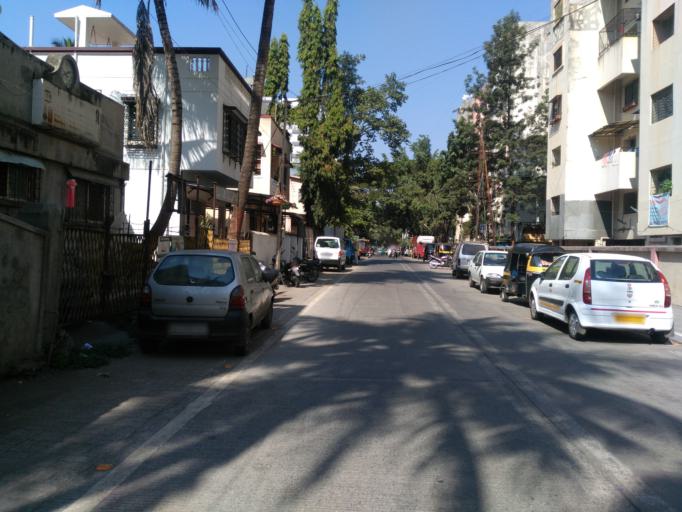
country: IN
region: Maharashtra
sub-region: Pune Division
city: Pune
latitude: 18.4837
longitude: 73.8517
